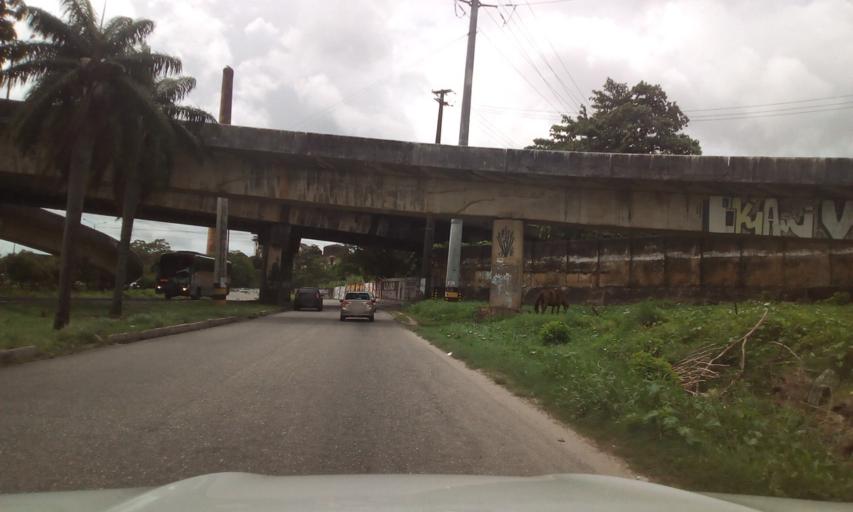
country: BR
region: Paraiba
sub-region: Joao Pessoa
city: Joao Pessoa
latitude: -7.1236
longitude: -34.8938
